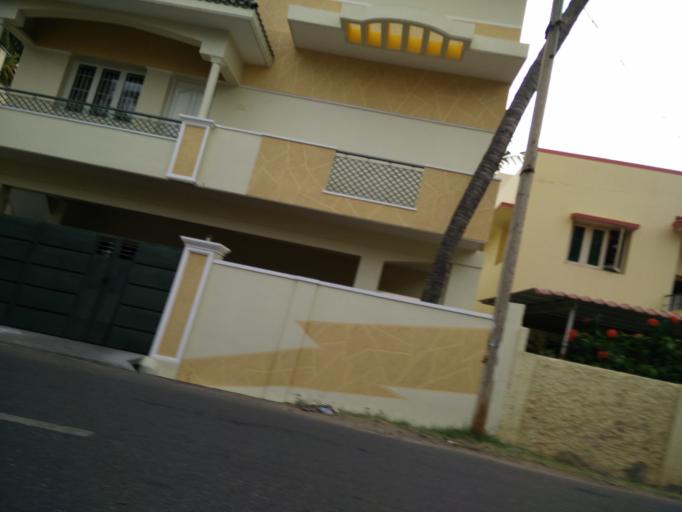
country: IN
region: Tamil Nadu
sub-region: Coimbatore
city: Coimbatore
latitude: 11.0273
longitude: 76.9417
